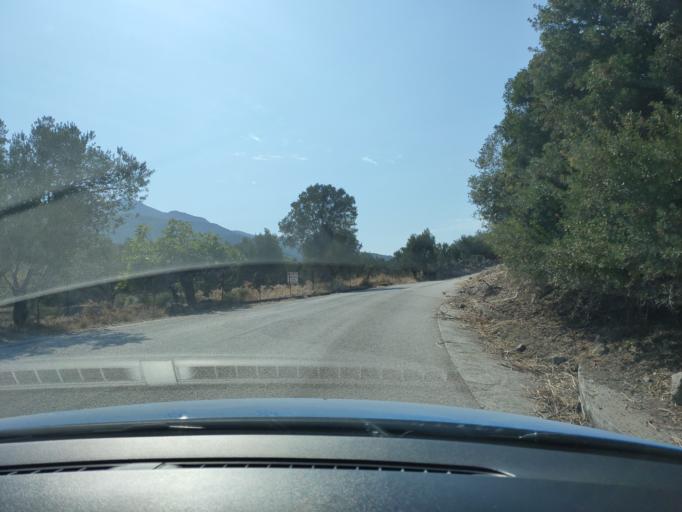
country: GR
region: North Aegean
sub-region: Nomos Lesvou
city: Mantamados
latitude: 39.3735
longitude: 26.3085
